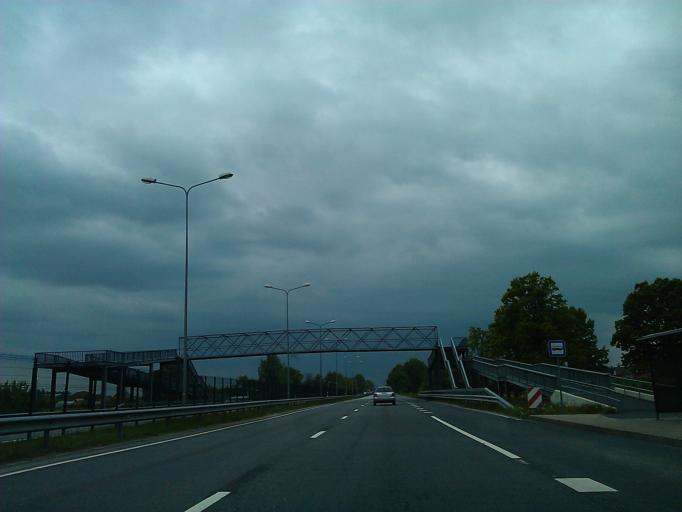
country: LV
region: Olaine
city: Olaine
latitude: 56.8070
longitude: 23.9936
